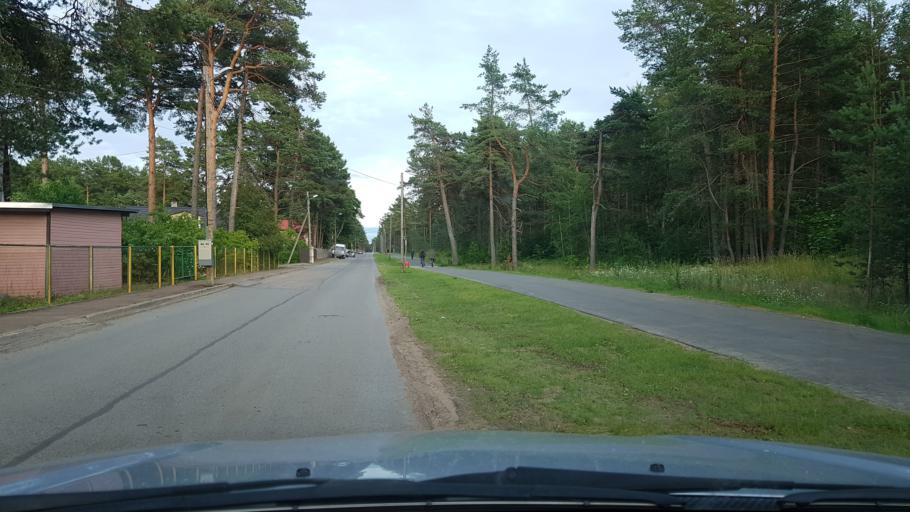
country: EE
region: Ida-Virumaa
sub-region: Narva-Joesuu linn
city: Narva-Joesuu
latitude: 59.4549
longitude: 28.0477
